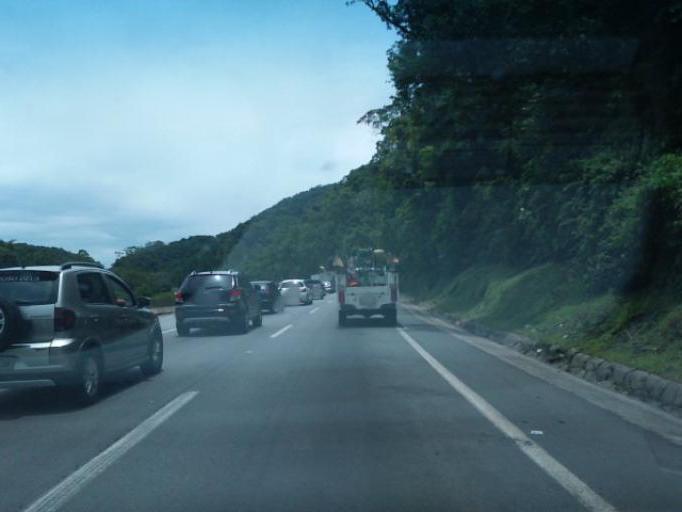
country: BR
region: Sao Paulo
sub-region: Juquitiba
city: Juquitiba
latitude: -24.0516
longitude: -47.2032
